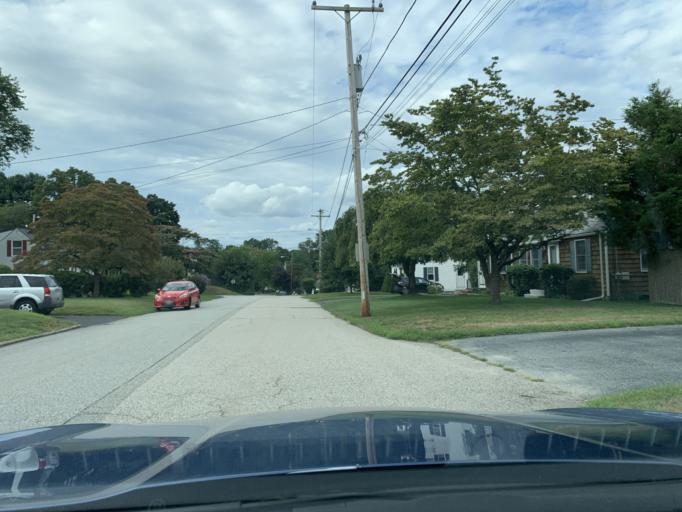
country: US
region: Rhode Island
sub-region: Kent County
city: East Greenwich
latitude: 41.6438
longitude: -71.4559
